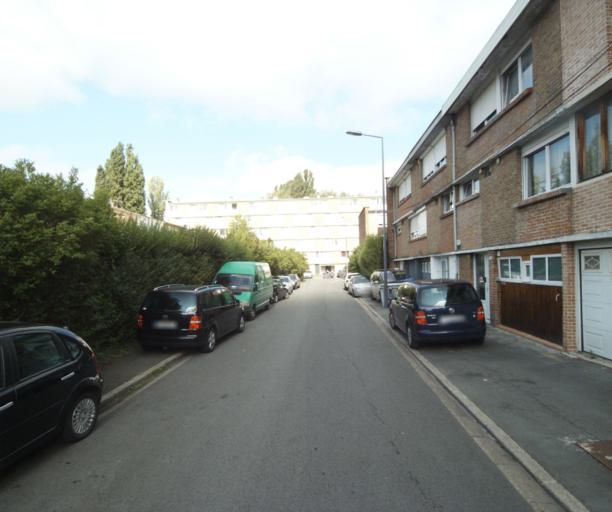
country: FR
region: Nord-Pas-de-Calais
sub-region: Departement du Nord
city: Mons-en-Baroeul
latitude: 50.6225
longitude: 3.1407
